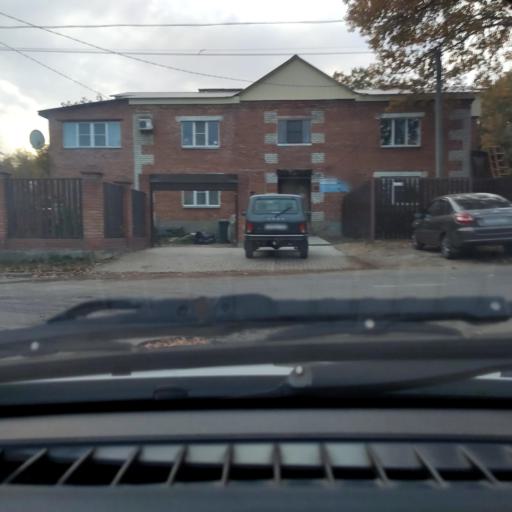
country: RU
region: Samara
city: Tol'yatti
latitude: 53.5329
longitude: 49.3889
